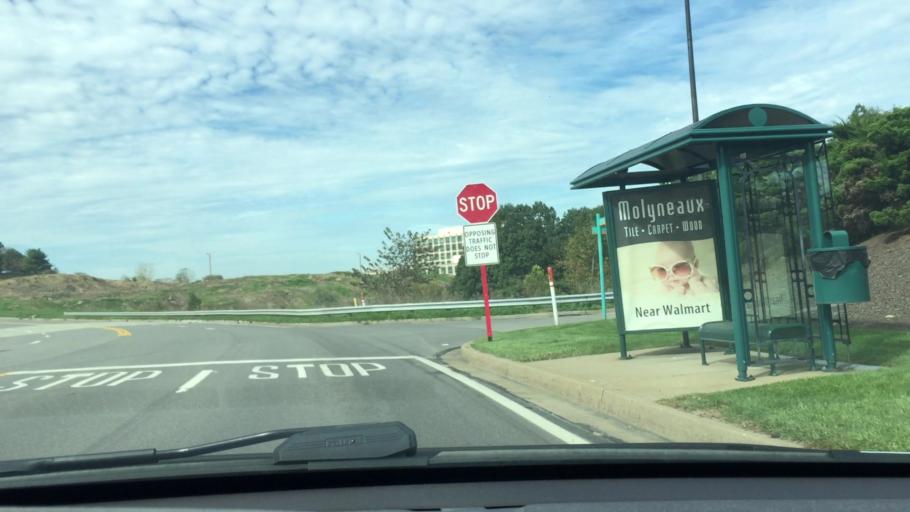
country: US
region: Pennsylvania
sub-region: Allegheny County
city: Enlow
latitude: 40.4510
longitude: -80.1845
